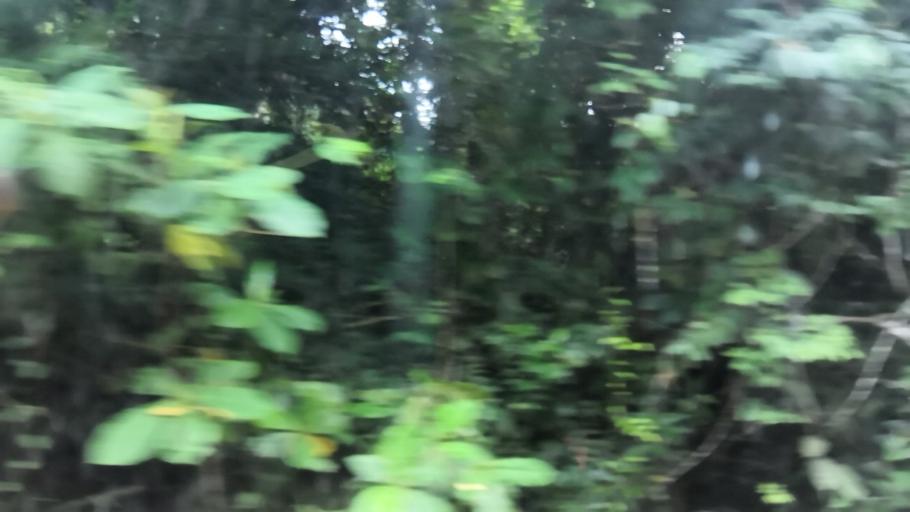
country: MY
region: Perak
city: Lumut
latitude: 4.2391
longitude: 100.5467
